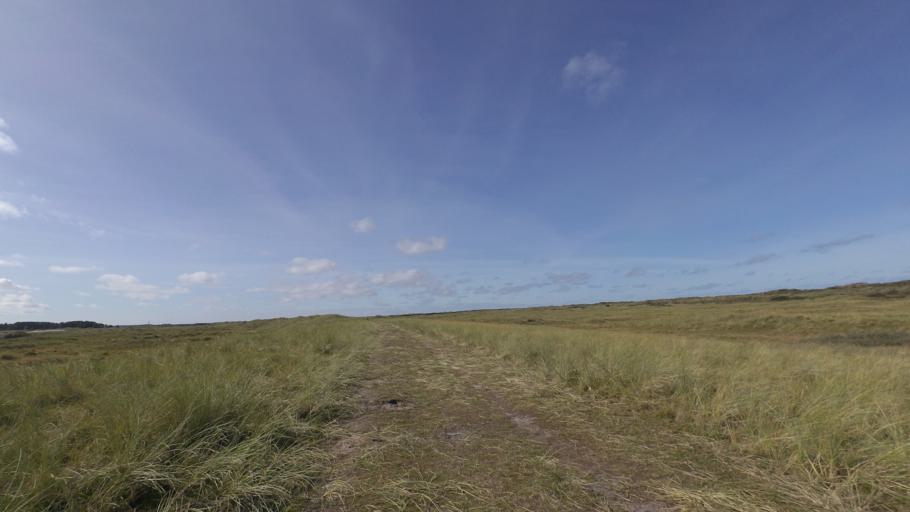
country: NL
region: Friesland
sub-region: Gemeente Ameland
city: Nes
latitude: 53.4546
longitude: 5.7079
